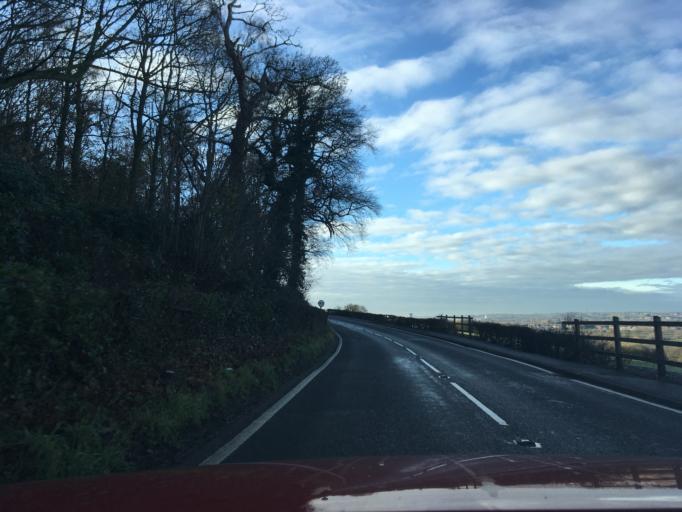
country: GB
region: England
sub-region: Staffordshire
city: Burton upon Trent
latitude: 52.8256
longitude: -1.6001
